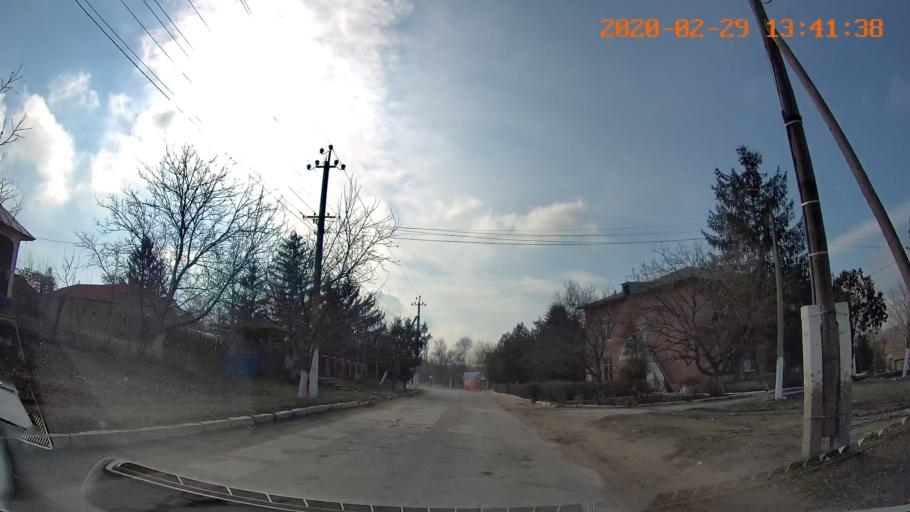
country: MD
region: Floresti
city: Leninskiy
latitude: 47.8446
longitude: 28.5565
